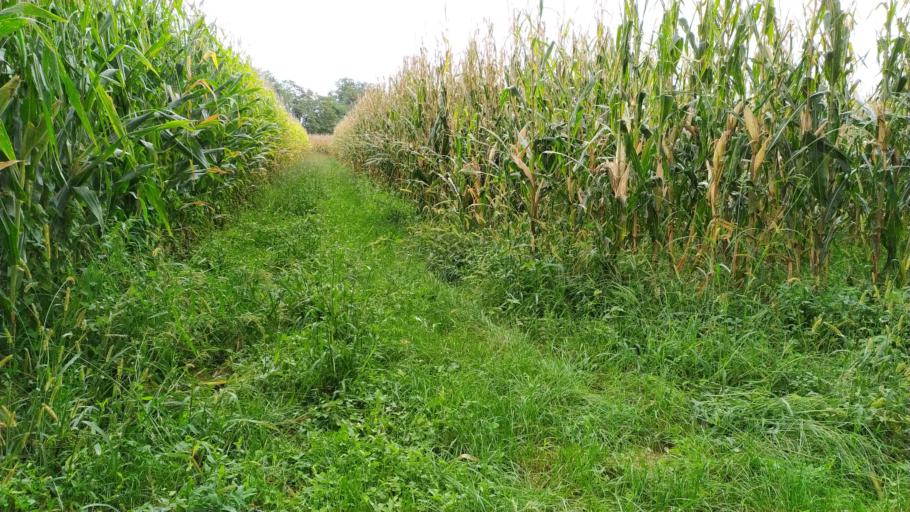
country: IT
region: Veneto
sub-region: Provincia di Vicenza
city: Giavenale
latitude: 45.6841
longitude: 11.4069
